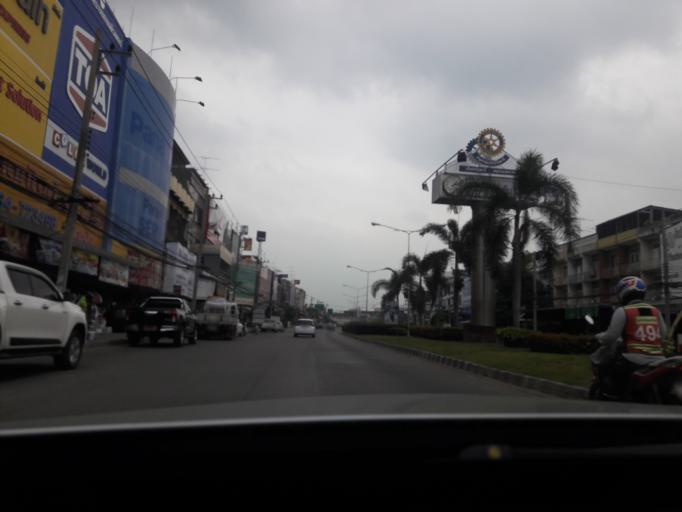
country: TH
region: Samut Songkhram
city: Samut Songkhram
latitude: 13.4039
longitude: 100.0023
